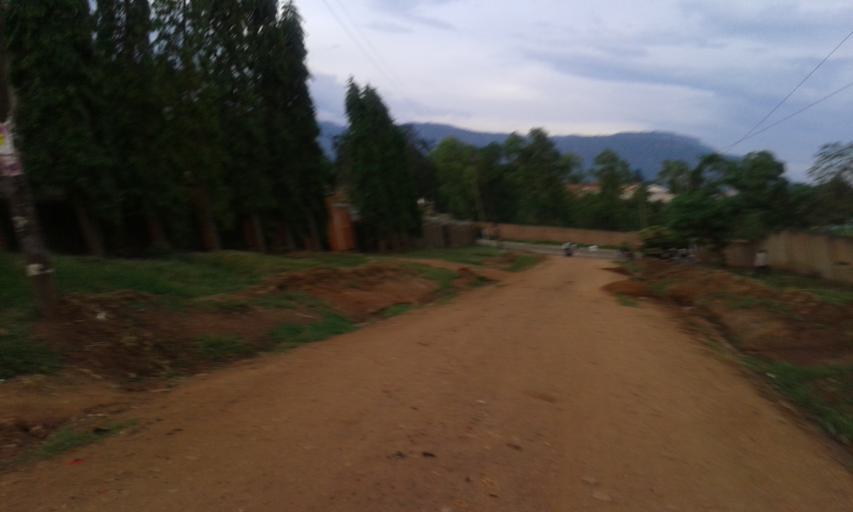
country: UG
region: Eastern Region
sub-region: Mbale District
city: Mbale
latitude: 1.0802
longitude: 34.1737
